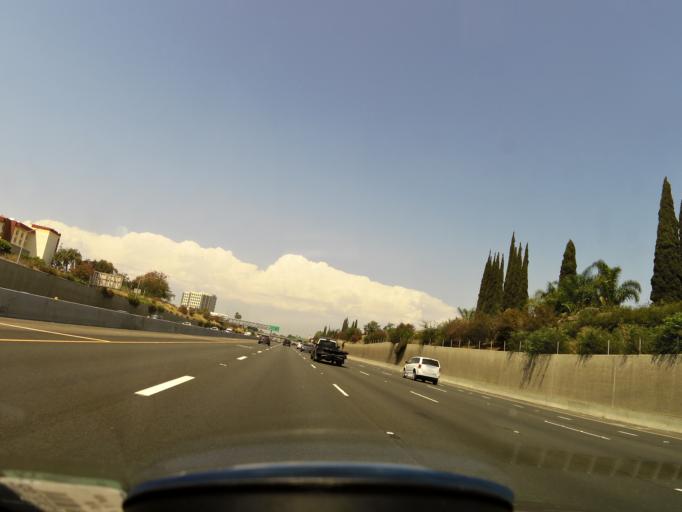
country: US
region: California
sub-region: Orange County
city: Tustin
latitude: 33.7519
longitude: -117.8315
